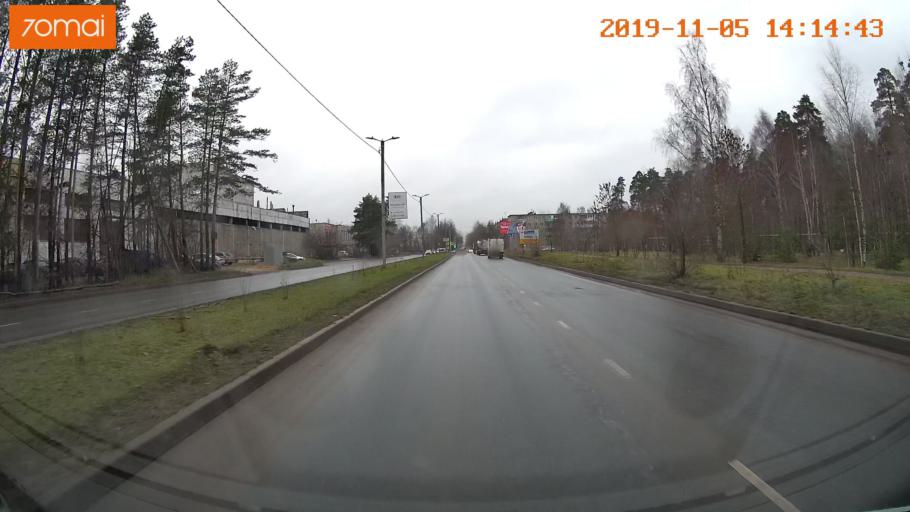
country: RU
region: Ivanovo
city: Kokhma
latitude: 56.9700
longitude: 41.0549
